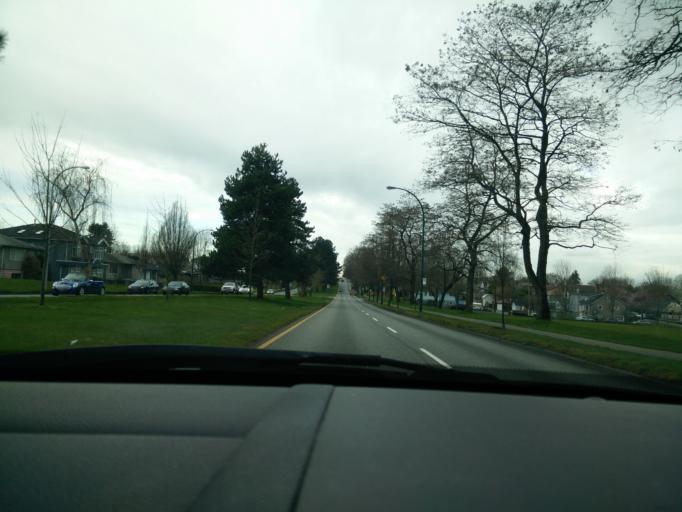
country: CA
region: British Columbia
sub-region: Fraser Valley Regional District
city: North Vancouver
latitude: 49.2696
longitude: -123.0500
